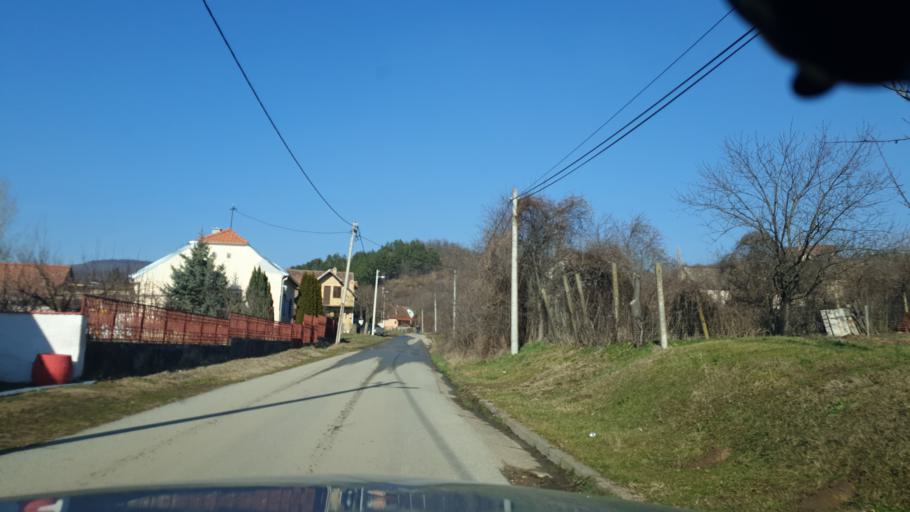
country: RS
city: Vrdnik
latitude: 45.1115
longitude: 19.7667
